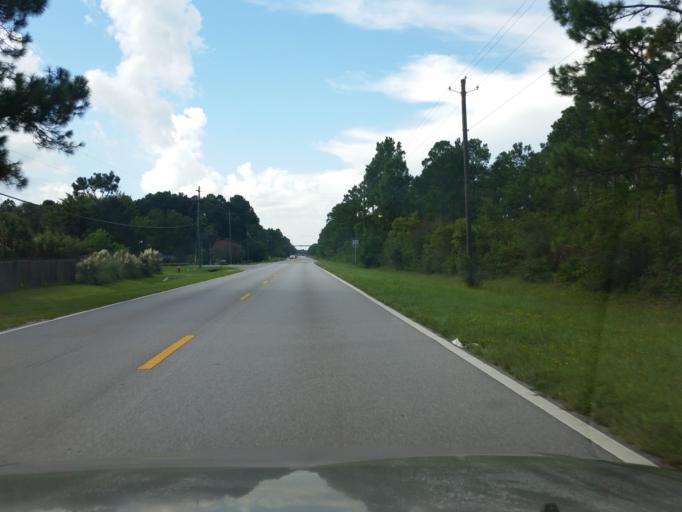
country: US
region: Florida
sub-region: Escambia County
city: Myrtle Grove
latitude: 30.3876
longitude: -87.4022
